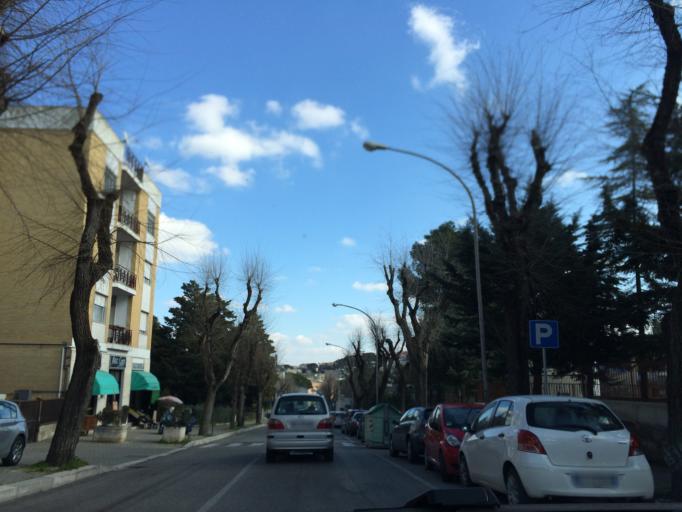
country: IT
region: Basilicate
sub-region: Provincia di Matera
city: Matera
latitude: 40.6647
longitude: 16.5947
